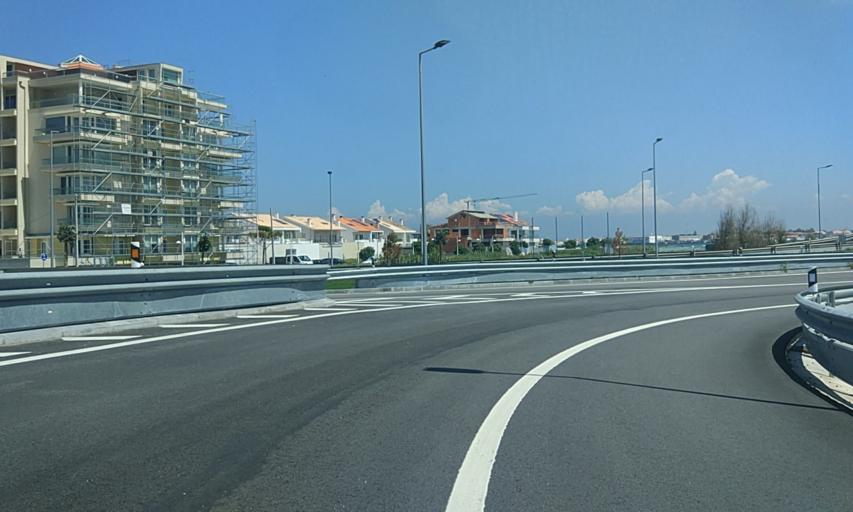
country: PT
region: Aveiro
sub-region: Ilhavo
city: Gafanha da Encarnacao
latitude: 40.6322
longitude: -8.7462
